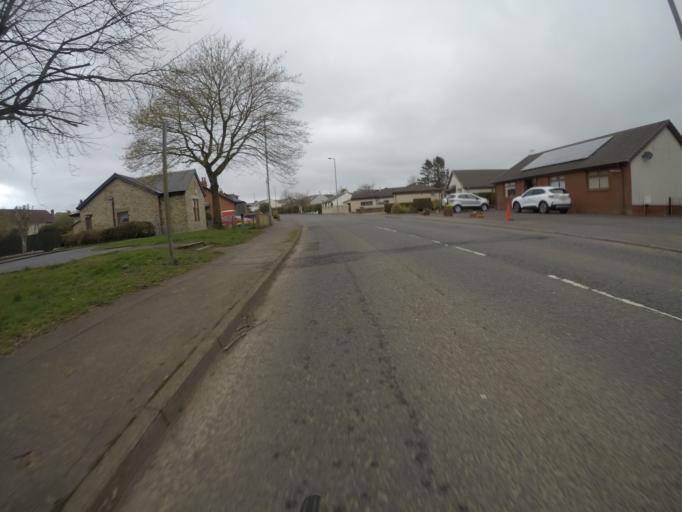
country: GB
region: Scotland
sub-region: North Ayrshire
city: Springside
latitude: 55.6138
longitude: -4.5860
